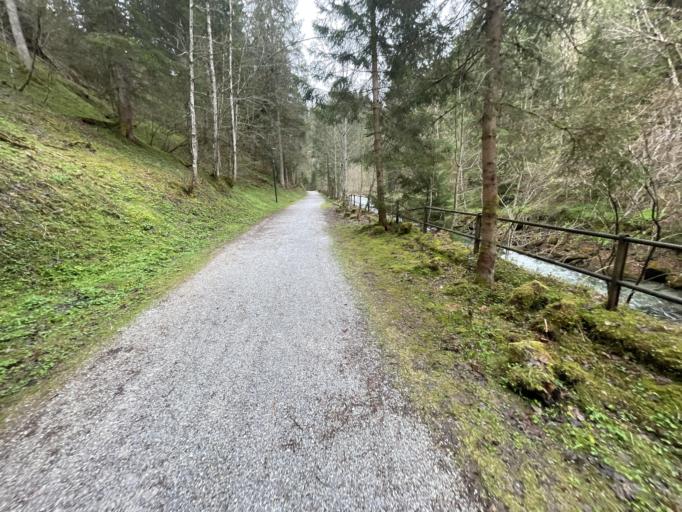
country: AT
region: Styria
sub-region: Politischer Bezirk Liezen
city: Schladming
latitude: 47.3837
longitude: 13.6832
